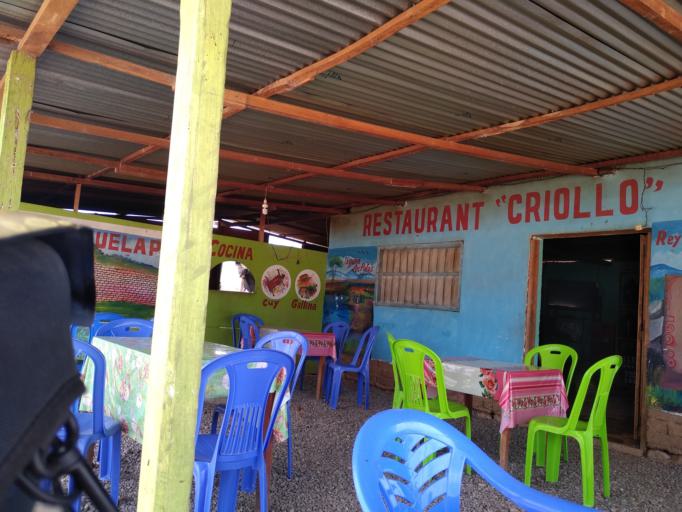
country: PE
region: Cajamarca
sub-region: Provincia de Jaen
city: Bellavista
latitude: -5.7353
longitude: -78.6443
